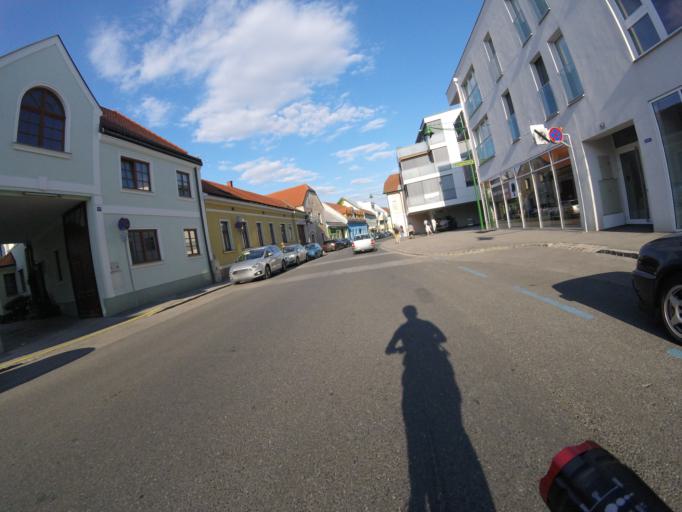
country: AT
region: Lower Austria
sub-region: Politischer Bezirk Modling
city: Guntramsdorf
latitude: 48.0492
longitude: 16.3141
